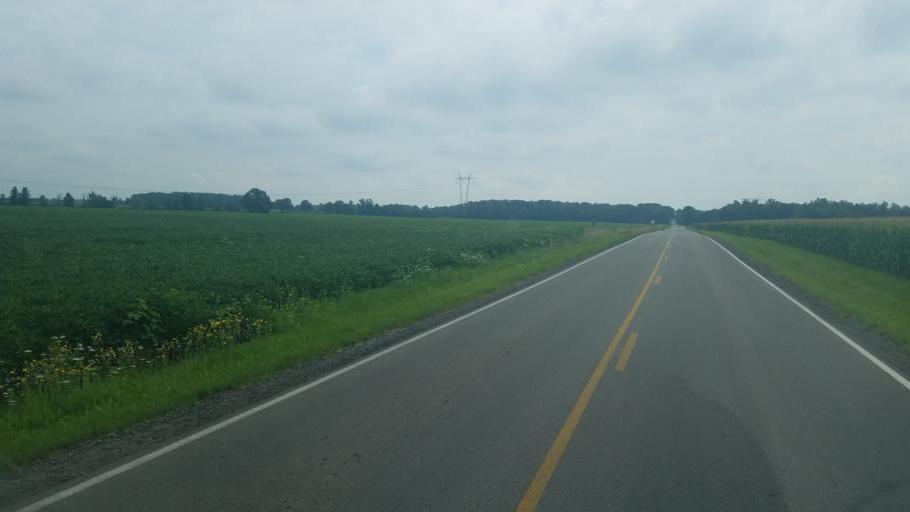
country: US
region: Ohio
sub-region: Crawford County
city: Galion
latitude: 40.7194
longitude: -82.8856
